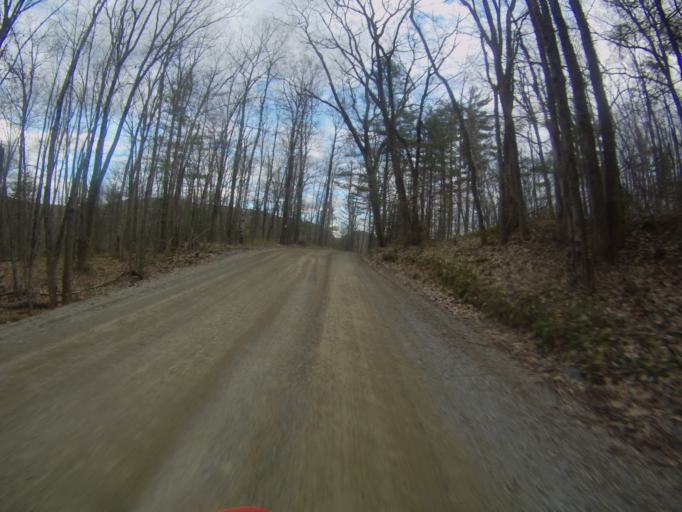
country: US
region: Vermont
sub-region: Addison County
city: Middlebury (village)
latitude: 43.9778
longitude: -73.0651
